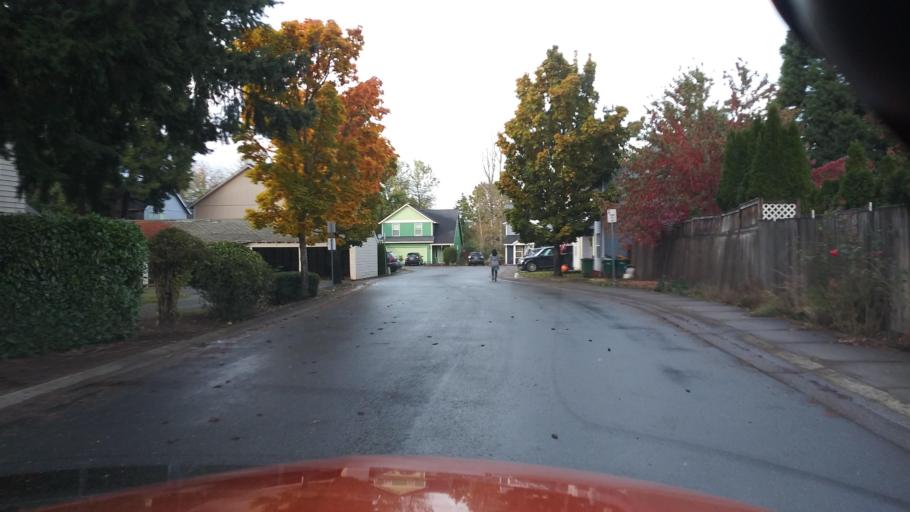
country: US
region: Oregon
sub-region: Washington County
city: Forest Grove
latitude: 45.5209
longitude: -123.1021
